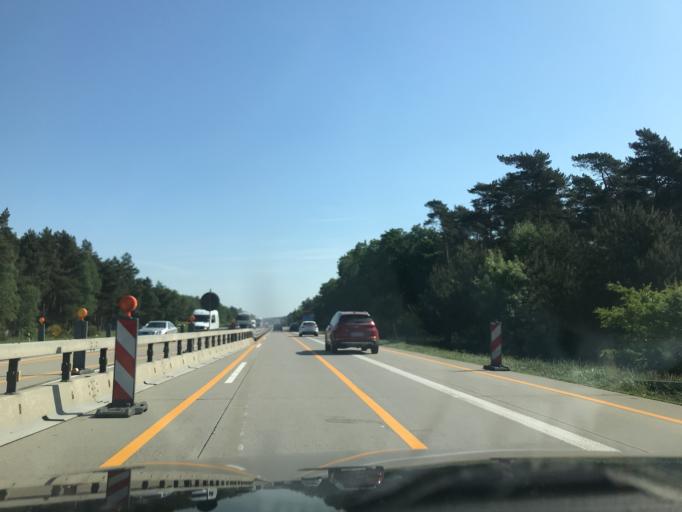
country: DE
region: Saxony-Anhalt
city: Nudersdorf
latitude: 51.9903
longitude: 12.5415
